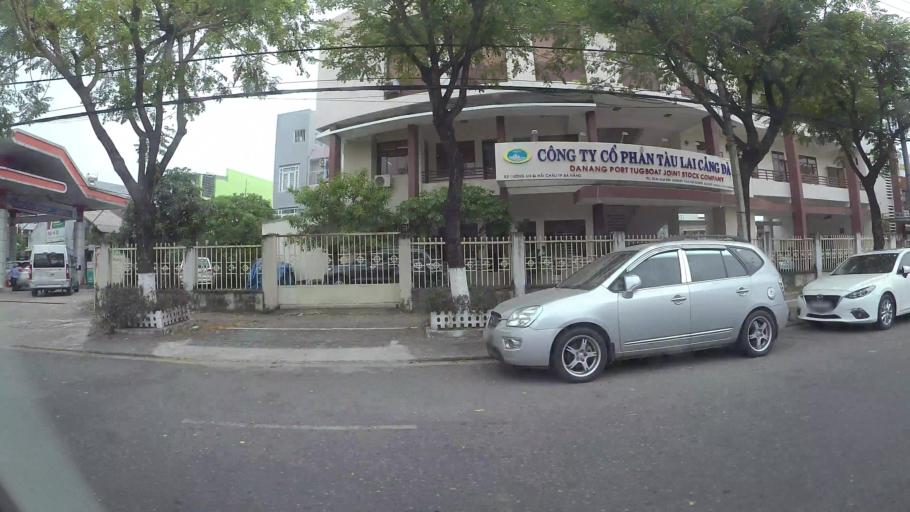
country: VN
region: Da Nang
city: Da Nang
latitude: 16.0832
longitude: 108.2222
